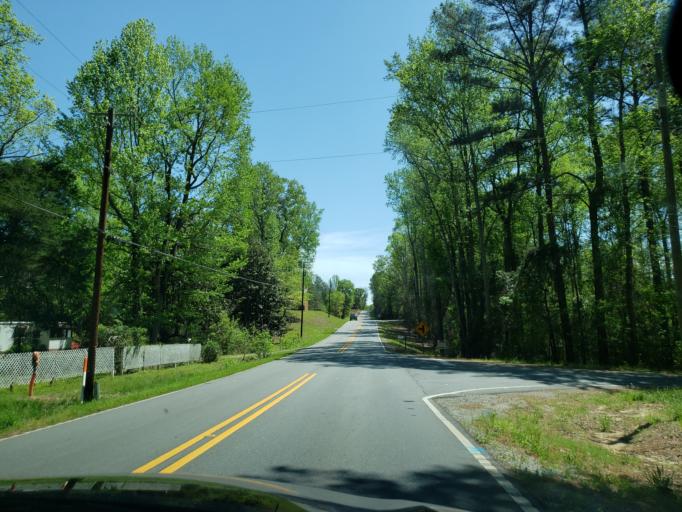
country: US
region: Alabama
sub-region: Tallapoosa County
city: Dadeville
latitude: 32.7022
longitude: -85.7501
